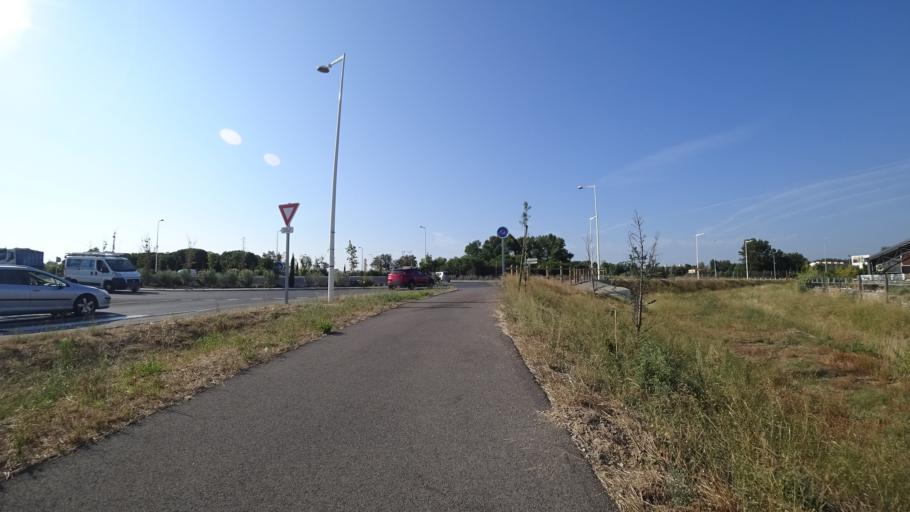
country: FR
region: Languedoc-Roussillon
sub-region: Departement des Pyrenees-Orientales
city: Perpignan
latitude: 42.7098
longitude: 2.9077
